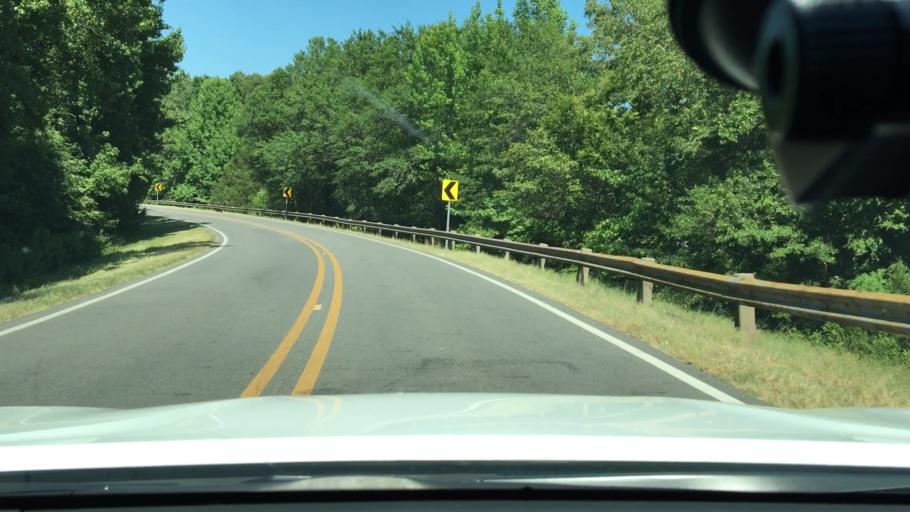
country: US
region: Arkansas
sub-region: Johnson County
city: Clarksville
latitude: 35.3574
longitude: -93.5495
